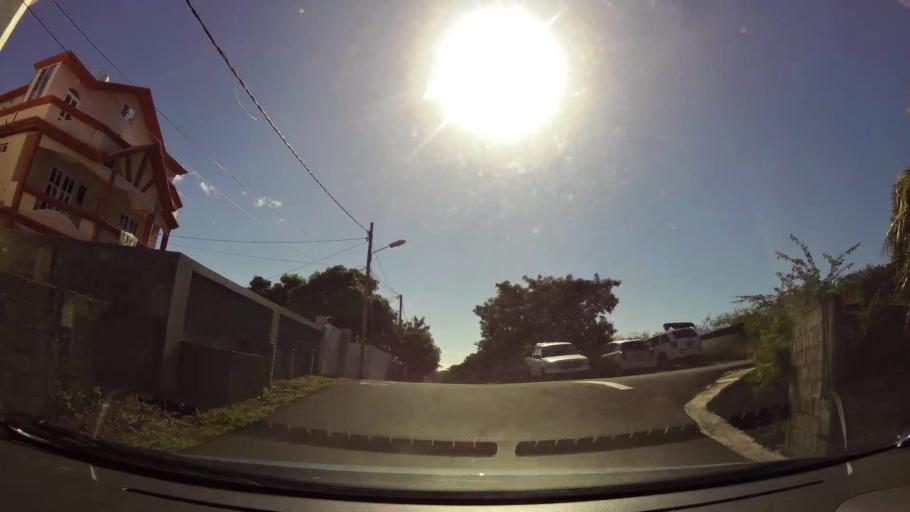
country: MU
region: Black River
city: Flic en Flac
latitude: -20.2681
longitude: 57.3751
